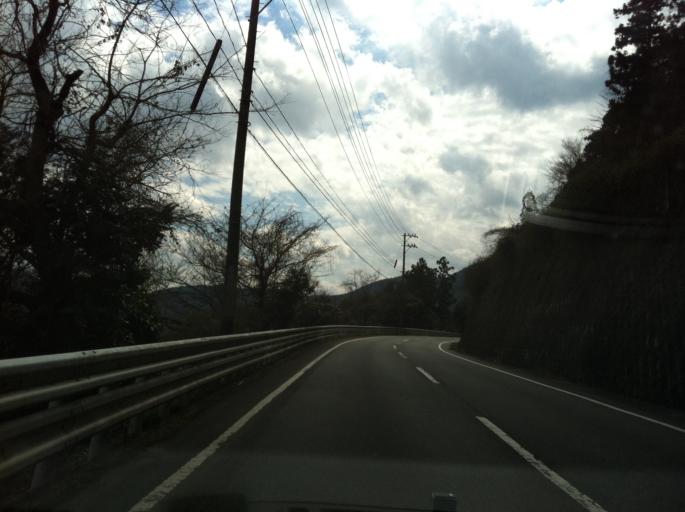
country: JP
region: Shizuoka
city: Kanaya
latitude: 34.9296
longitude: 138.0791
